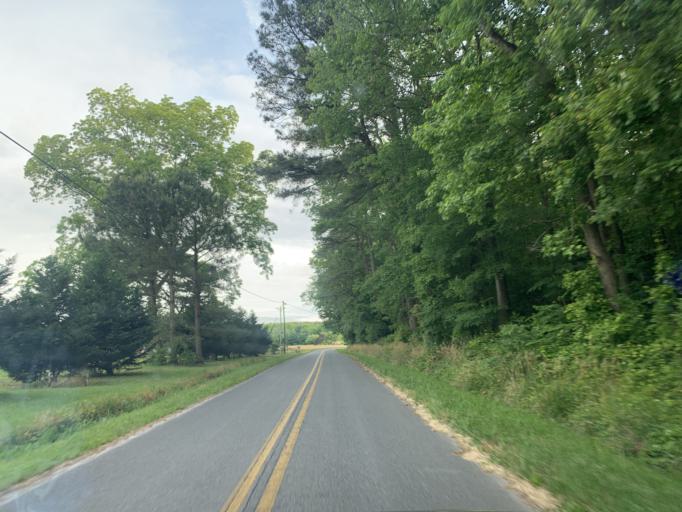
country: US
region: Maryland
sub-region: Worcester County
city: Pocomoke City
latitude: 38.0778
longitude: -75.4778
